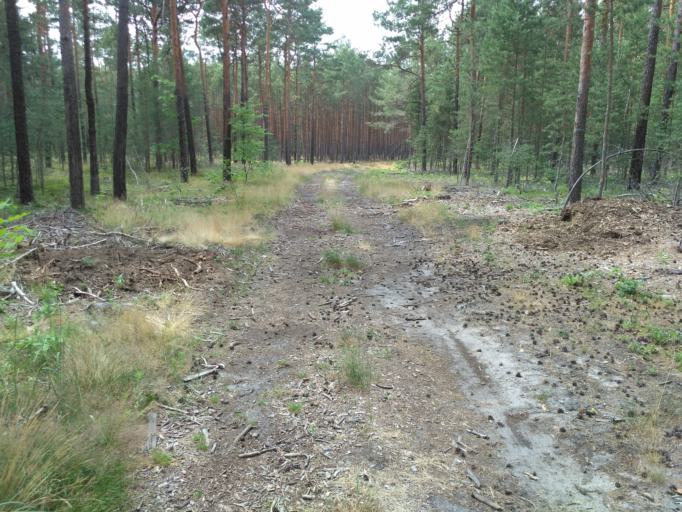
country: DE
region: Saxony
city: Hoyerswerda
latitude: 51.4543
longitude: 14.2837
